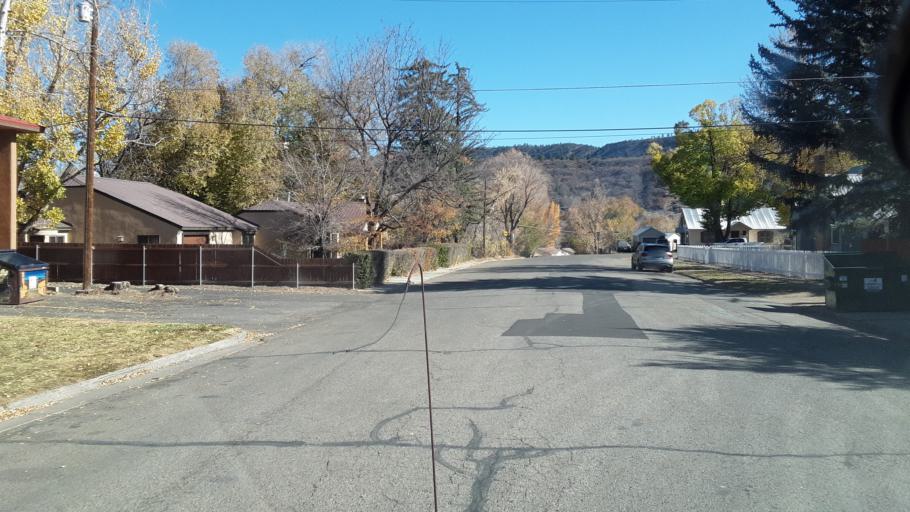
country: US
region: Colorado
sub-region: La Plata County
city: Durango
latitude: 37.2862
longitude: -107.8762
